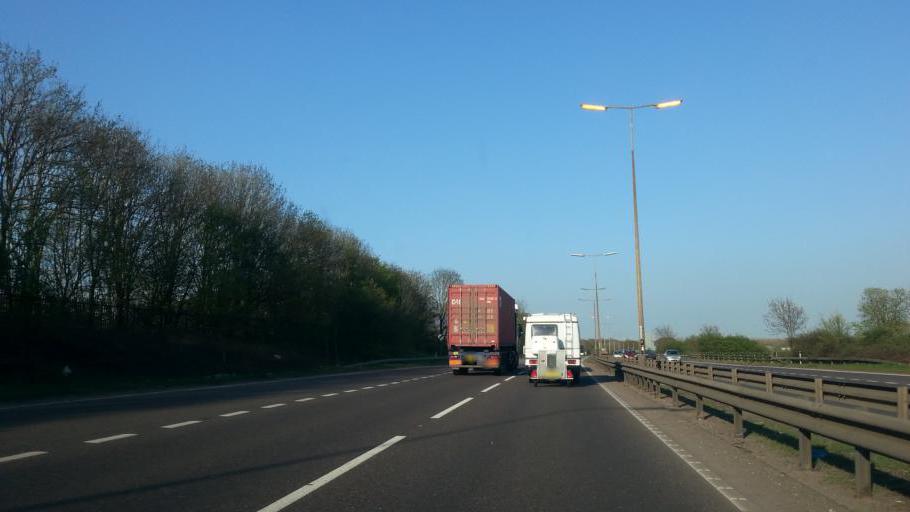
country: GB
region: England
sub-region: Northamptonshire
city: Earls Barton
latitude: 52.2531
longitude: -0.8029
